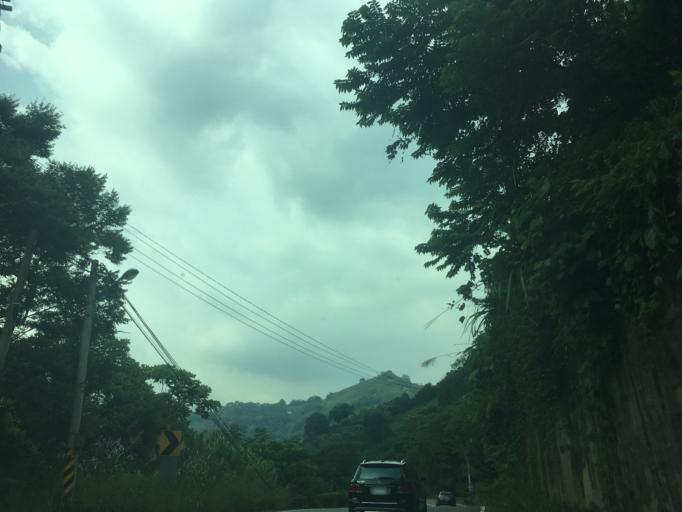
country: TW
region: Taiwan
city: Fengyuan
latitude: 24.3130
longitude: 120.9218
